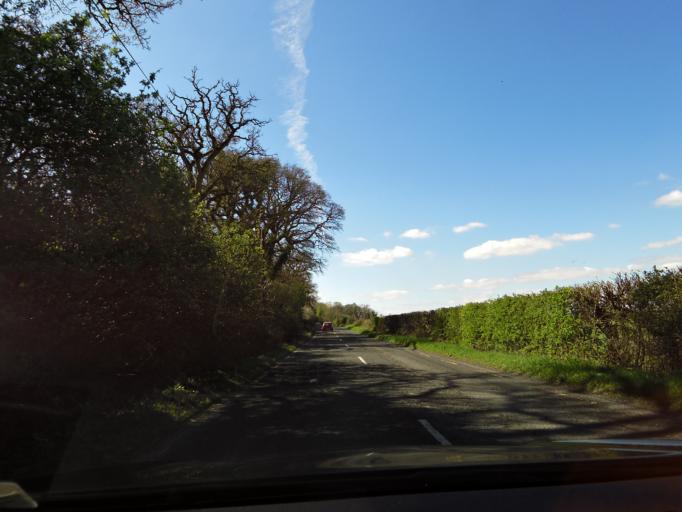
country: IE
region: Leinster
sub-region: Laois
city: Stradbally
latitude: 53.0170
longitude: -7.0915
